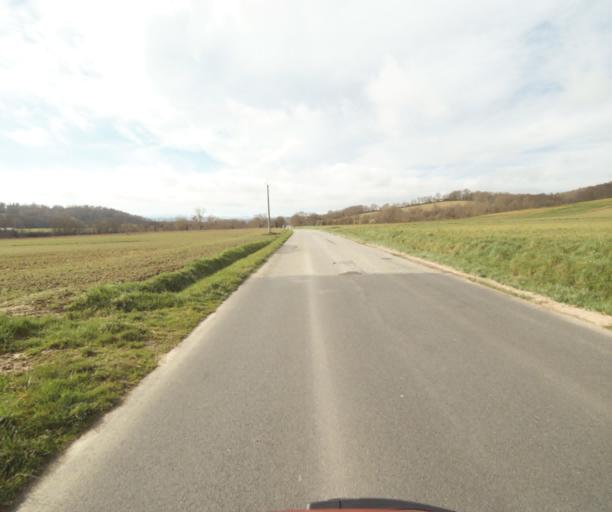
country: FR
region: Midi-Pyrenees
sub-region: Departement de l'Ariege
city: Pamiers
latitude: 43.1433
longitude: 1.5714
